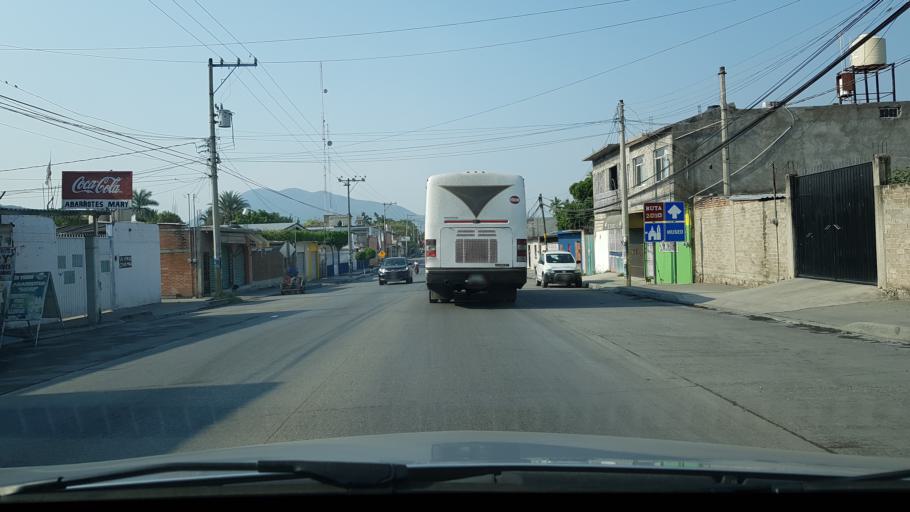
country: MX
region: Morelos
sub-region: Tlaquiltenango
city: Alfredo V. Bonfil (Chacampalco)
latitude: 18.6456
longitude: -99.1565
